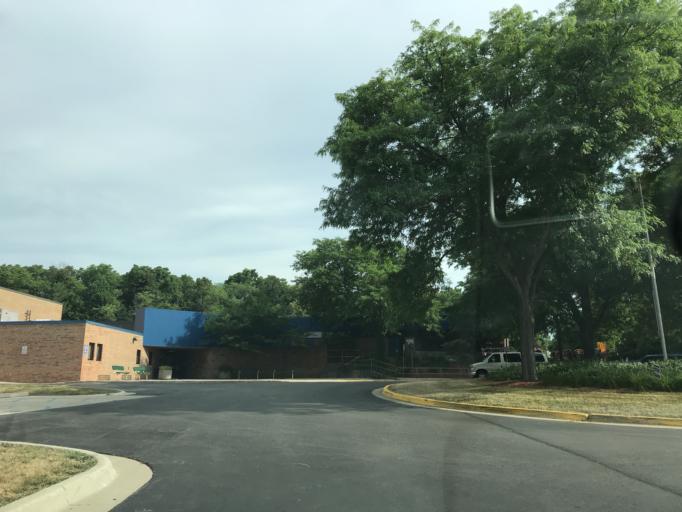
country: US
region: Michigan
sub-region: Washtenaw County
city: Ann Arbor
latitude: 42.2332
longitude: -83.7161
